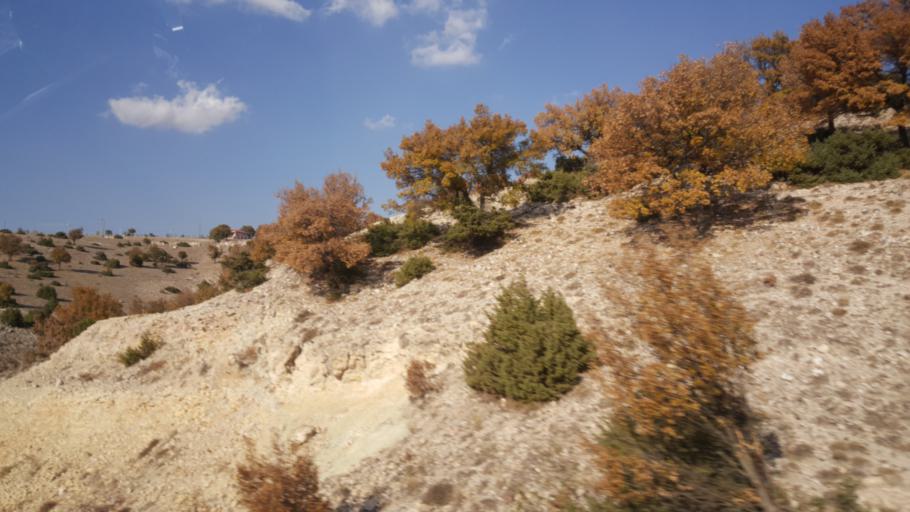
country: TR
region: Eskisehir
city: Kirka
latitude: 39.3244
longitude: 30.5673
